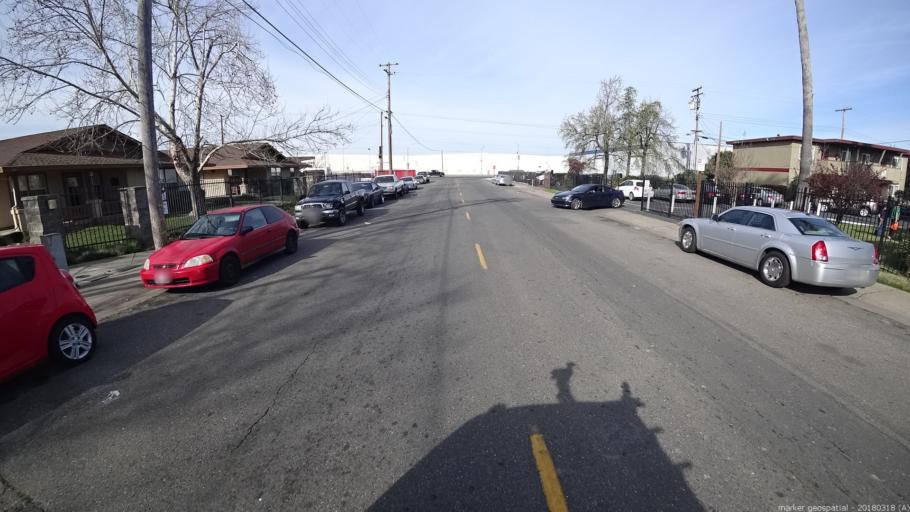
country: US
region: California
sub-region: Sacramento County
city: Parkway
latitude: 38.5158
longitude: -121.4679
